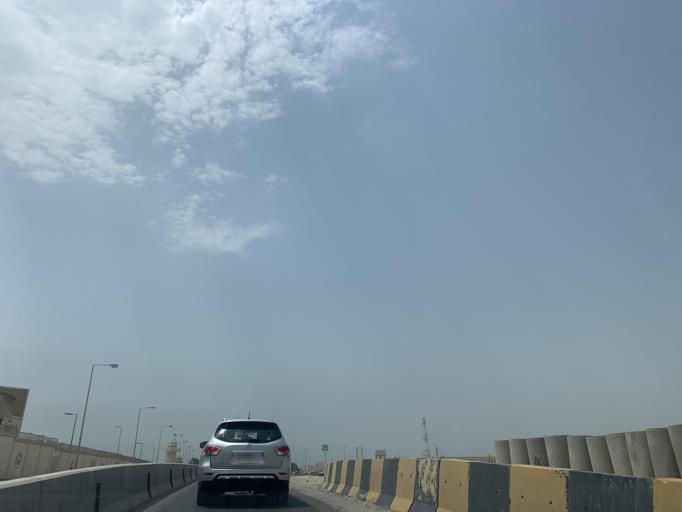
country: BH
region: Central Governorate
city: Madinat Hamad
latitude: 26.1520
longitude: 50.4842
